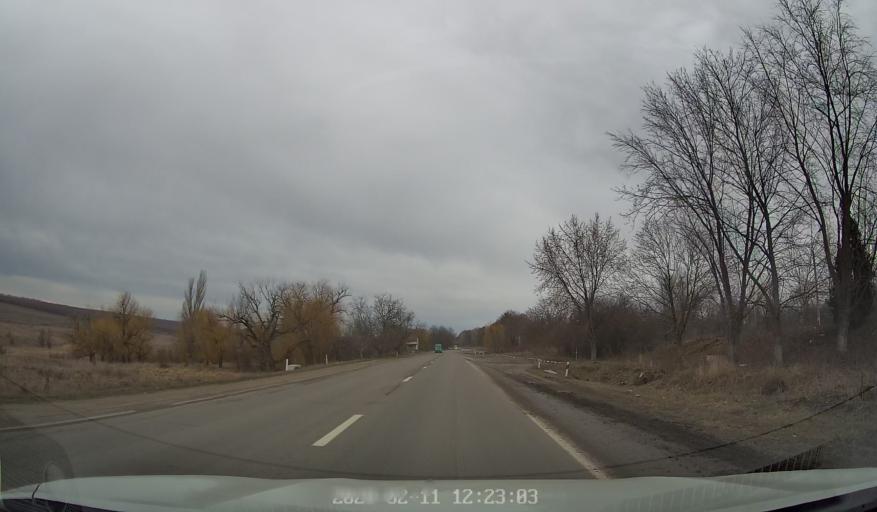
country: MD
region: Raionul Edinet
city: Edinet
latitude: 48.1329
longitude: 27.3613
